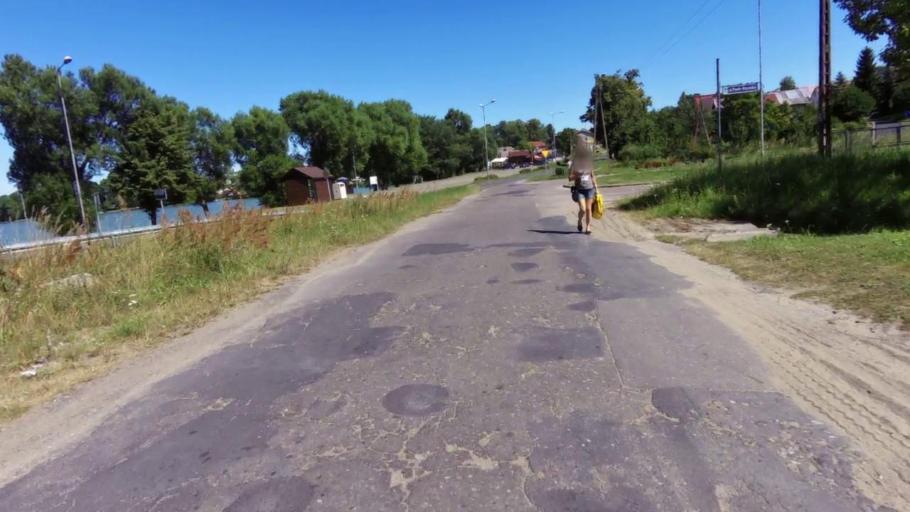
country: PL
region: West Pomeranian Voivodeship
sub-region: Powiat drawski
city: Czaplinek
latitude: 53.5545
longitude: 16.2277
